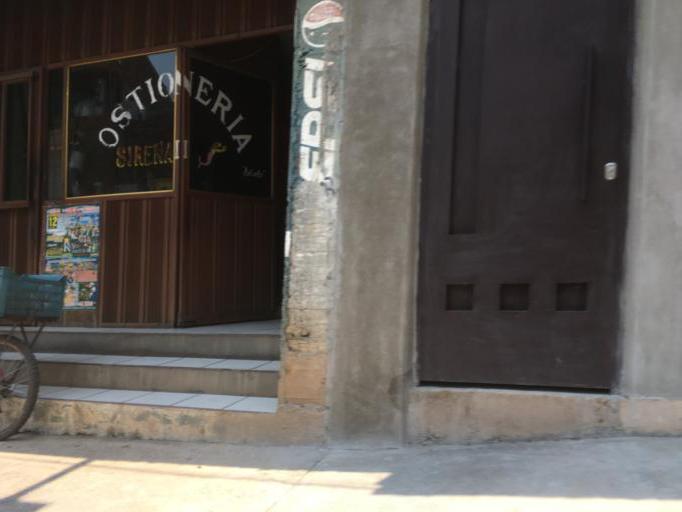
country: MX
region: Michoacan
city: Quiroga
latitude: 19.6604
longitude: -101.5221
